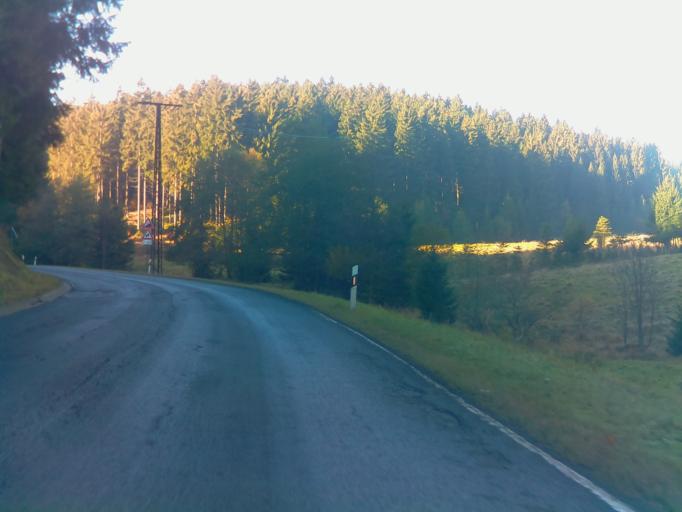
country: DE
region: Thuringia
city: Piesau
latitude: 50.5006
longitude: 11.2024
